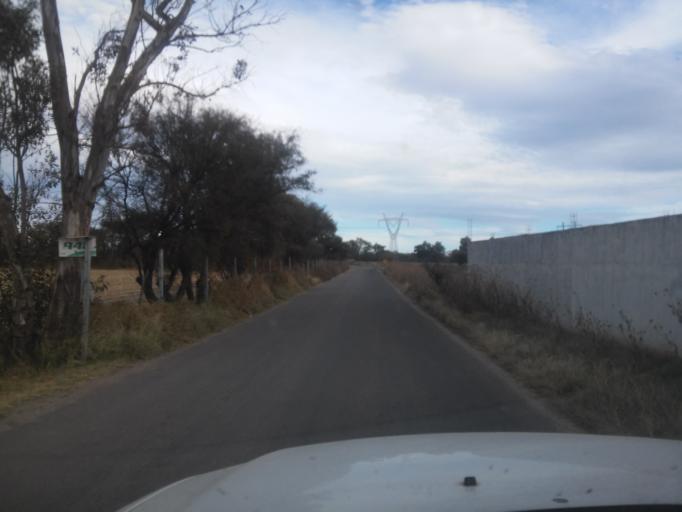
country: MX
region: Durango
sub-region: Durango
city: Jose Refugio Salcido
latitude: 24.0301
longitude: -104.5702
